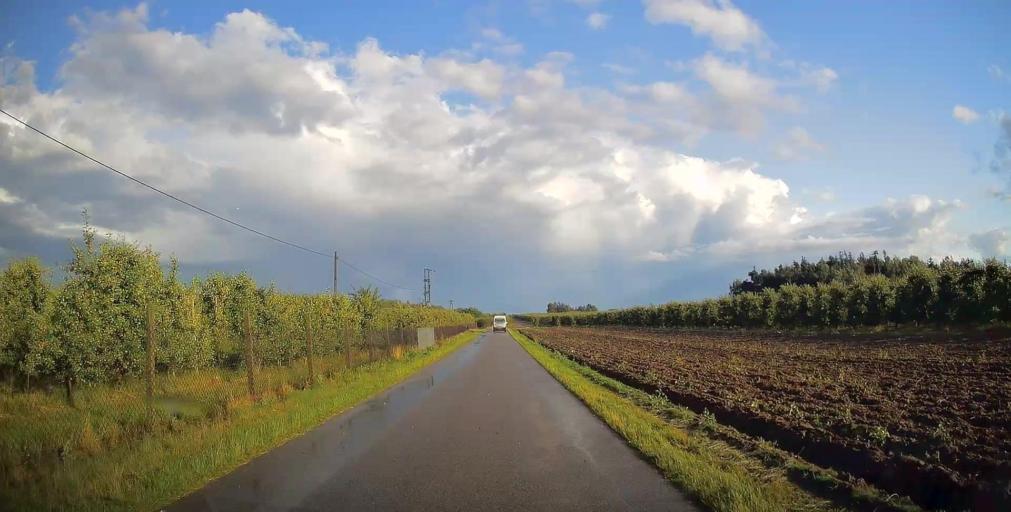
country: PL
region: Masovian Voivodeship
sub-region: Powiat grojecki
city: Goszczyn
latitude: 51.7502
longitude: 20.8854
